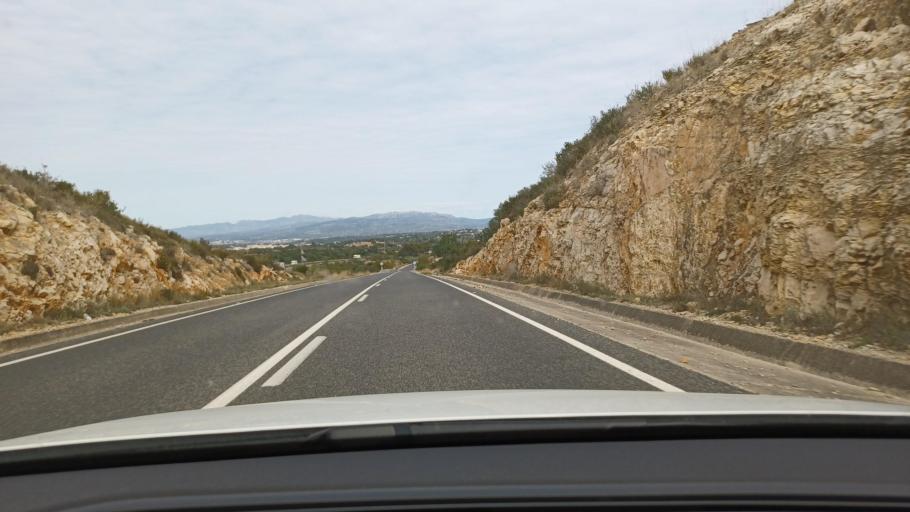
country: ES
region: Catalonia
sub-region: Provincia de Tarragona
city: Masdenverge
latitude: 40.6829
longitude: 0.5259
